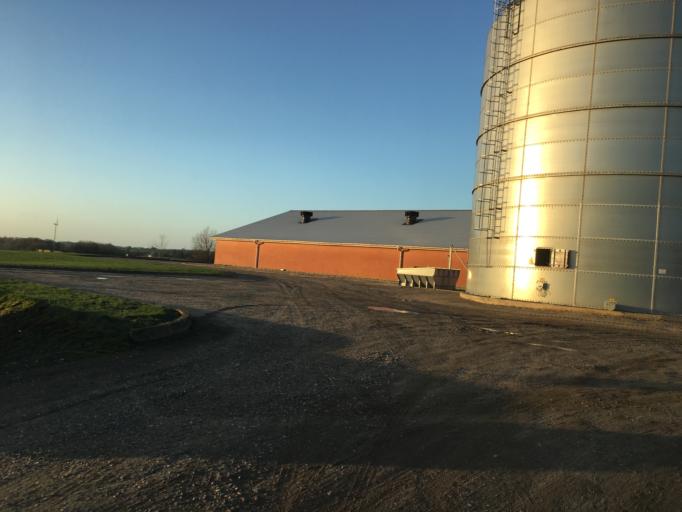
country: DK
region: North Denmark
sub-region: Bronderslev Kommune
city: Bronderslev
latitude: 57.2787
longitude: 10.0567
